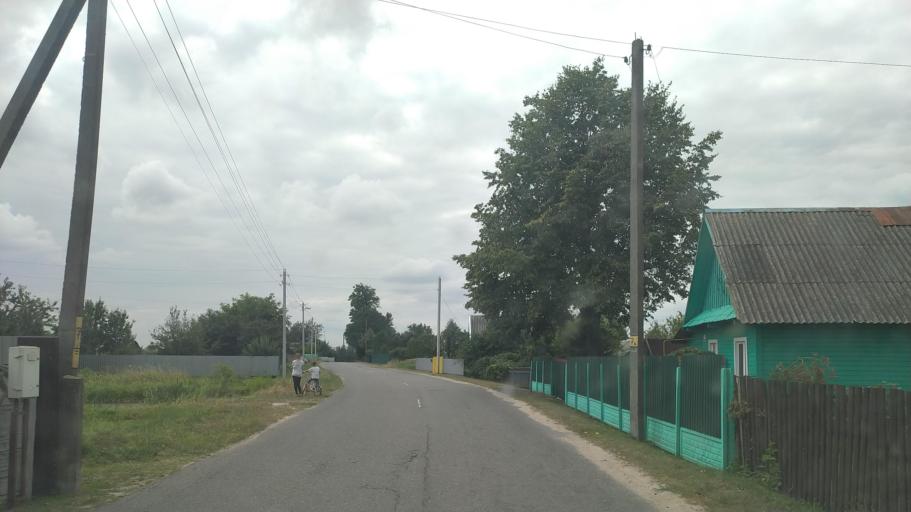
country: BY
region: Brest
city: Byelaazyorsk
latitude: 52.5429
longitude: 25.1082
